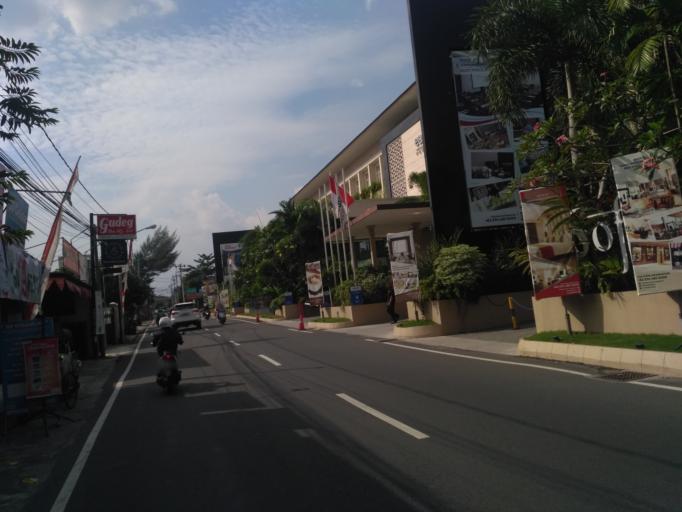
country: ID
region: Daerah Istimewa Yogyakarta
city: Depok
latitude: -7.7819
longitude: 110.4084
